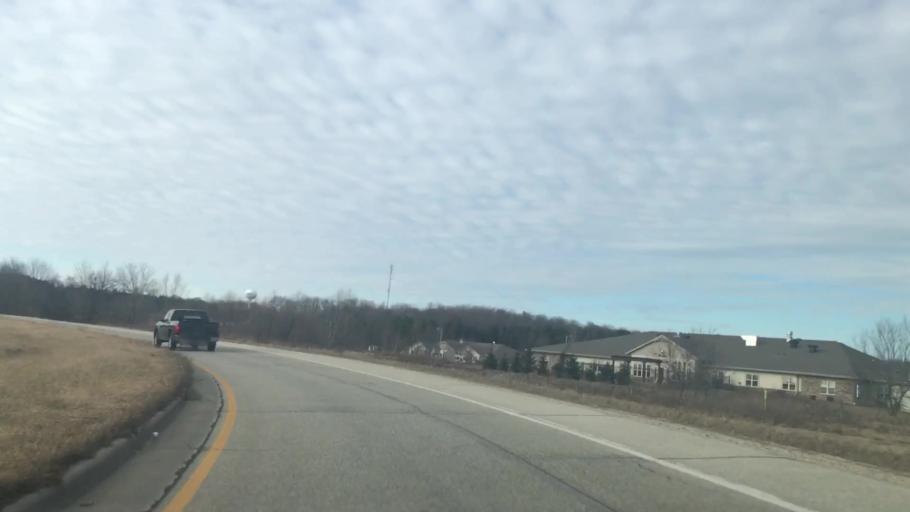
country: US
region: Wisconsin
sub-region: Washington County
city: Slinger
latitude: 43.3263
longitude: -88.2496
